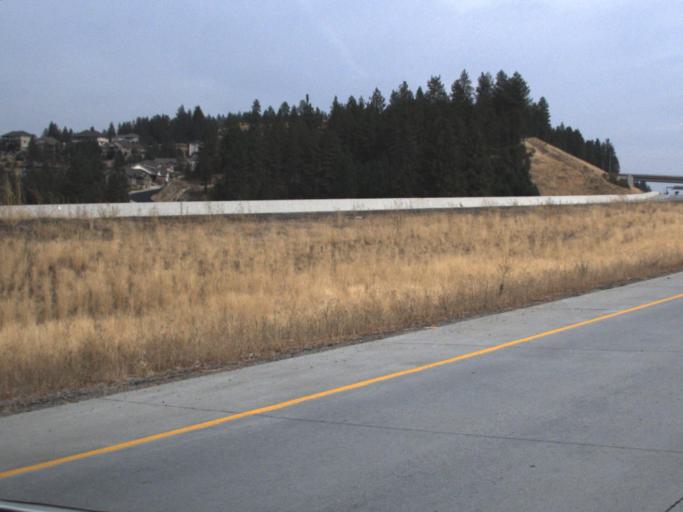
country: US
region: Washington
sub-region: Spokane County
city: Fairwood
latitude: 47.7789
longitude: -117.3985
